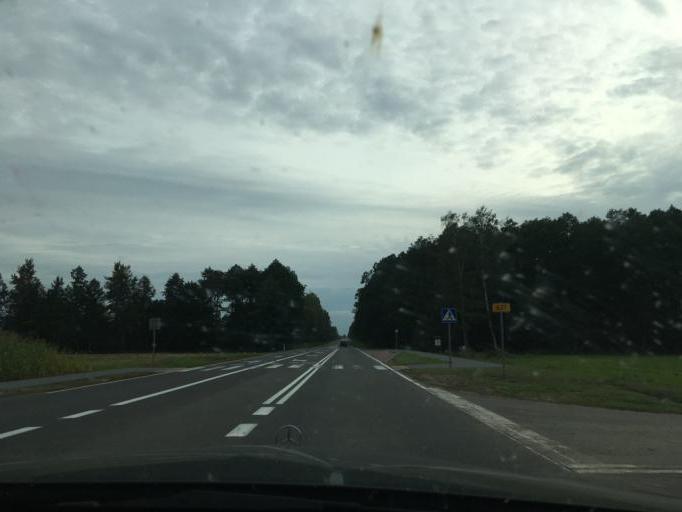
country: PL
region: Masovian Voivodeship
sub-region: Powiat ostrowski
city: Ostrow Mazowiecka
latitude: 52.8998
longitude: 21.8702
